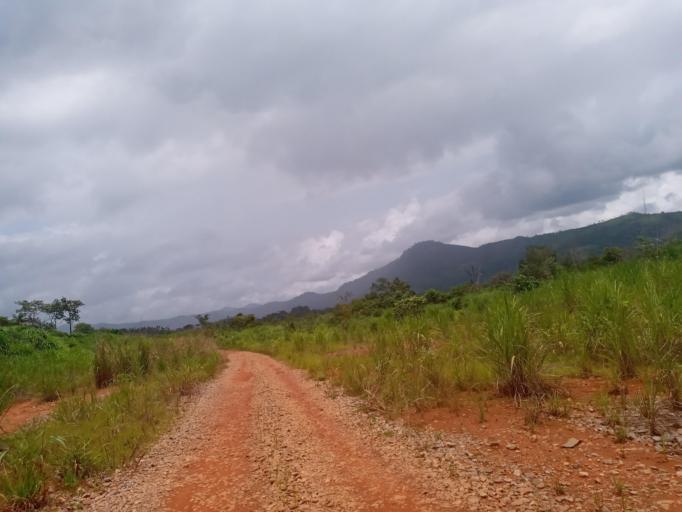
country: SL
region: Northern Province
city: Bumbuna
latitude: 8.9733
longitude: -11.7546
